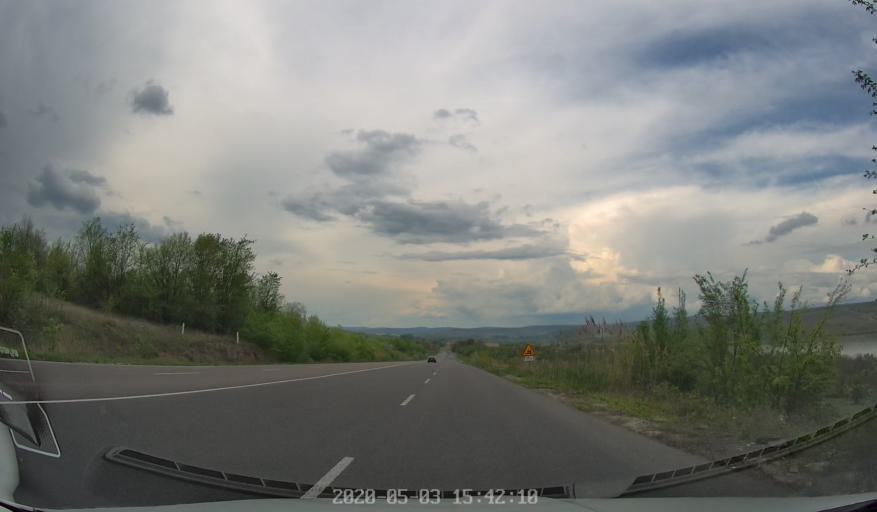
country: MD
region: Chisinau
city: Vatra
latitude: 47.1115
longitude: 28.6847
